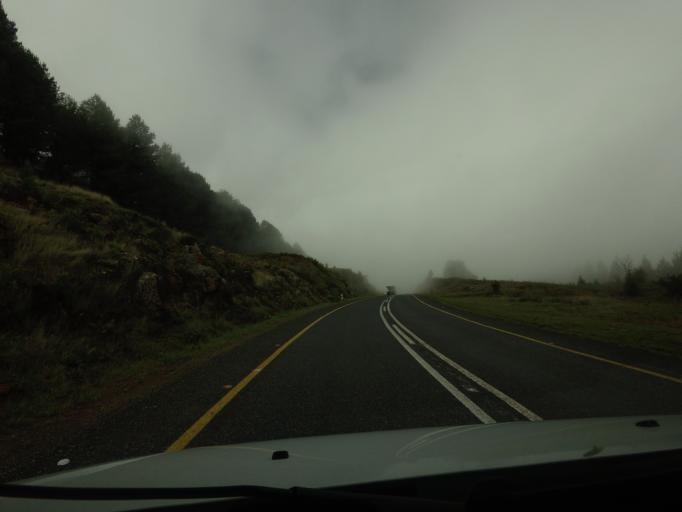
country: ZA
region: Mpumalanga
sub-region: Ehlanzeni District
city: Lydenburg
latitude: -25.1627
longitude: 30.6310
